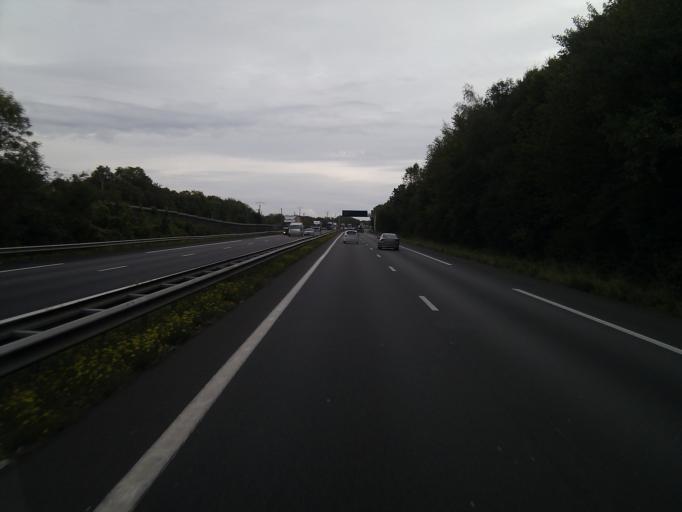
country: FR
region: Lorraine
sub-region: Departement de Meurthe-et-Moselle
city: Velaine-en-Haye
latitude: 48.6907
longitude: 6.0341
